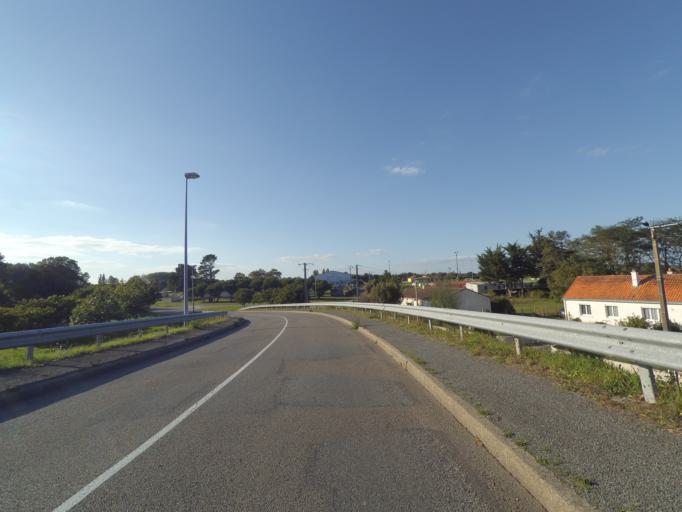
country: FR
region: Pays de la Loire
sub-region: Departement de la Loire-Atlantique
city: Chemere
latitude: 47.1267
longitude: -1.9196
